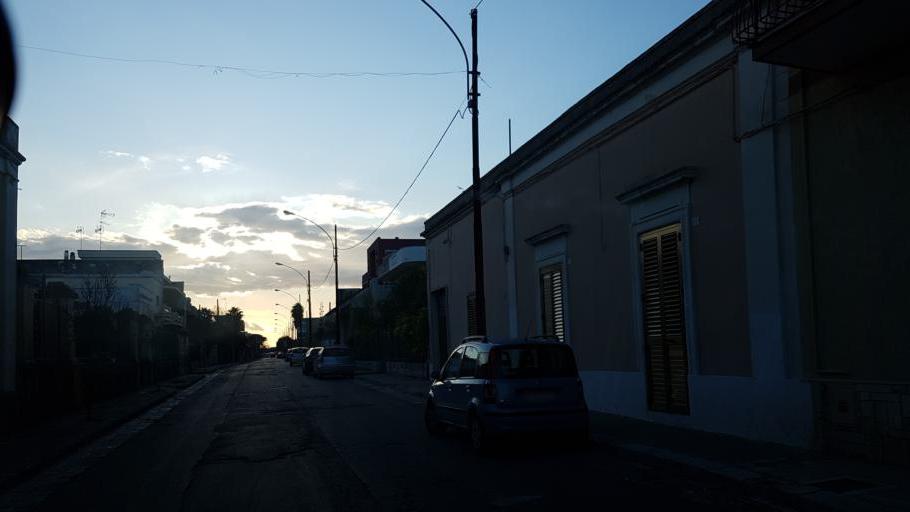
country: IT
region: Apulia
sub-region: Provincia di Lecce
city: Surbo
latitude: 40.3928
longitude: 18.1292
